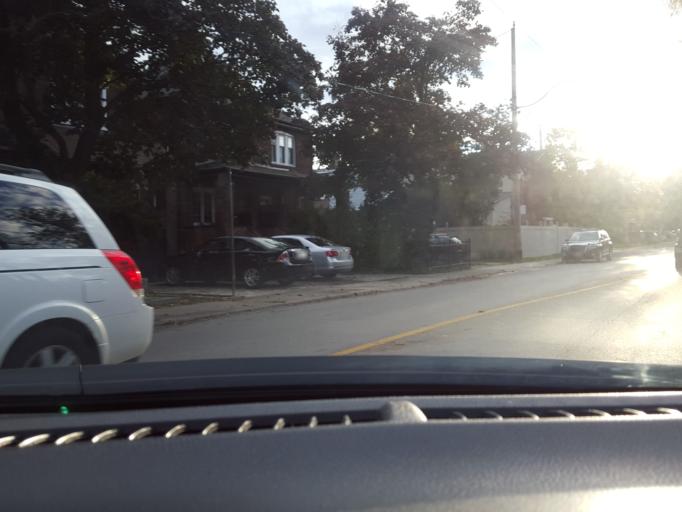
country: CA
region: Ontario
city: Toronto
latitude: 43.7022
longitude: -79.3781
